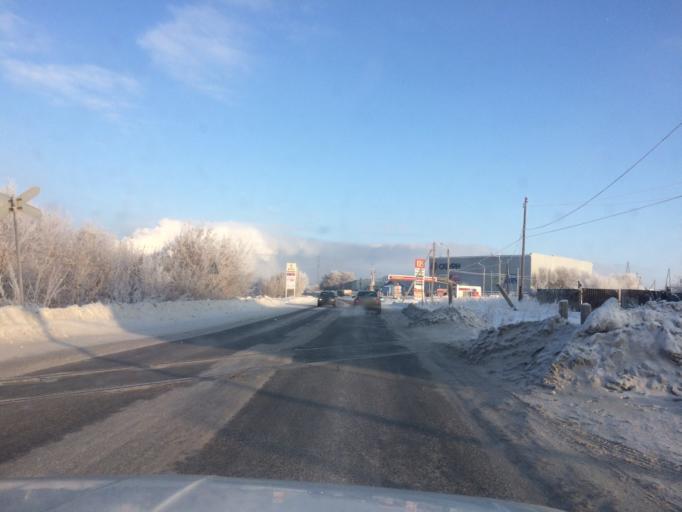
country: RU
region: Chelyabinsk
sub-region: Gorod Magnitogorsk
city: Magnitogorsk
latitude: 53.3967
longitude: 59.0858
